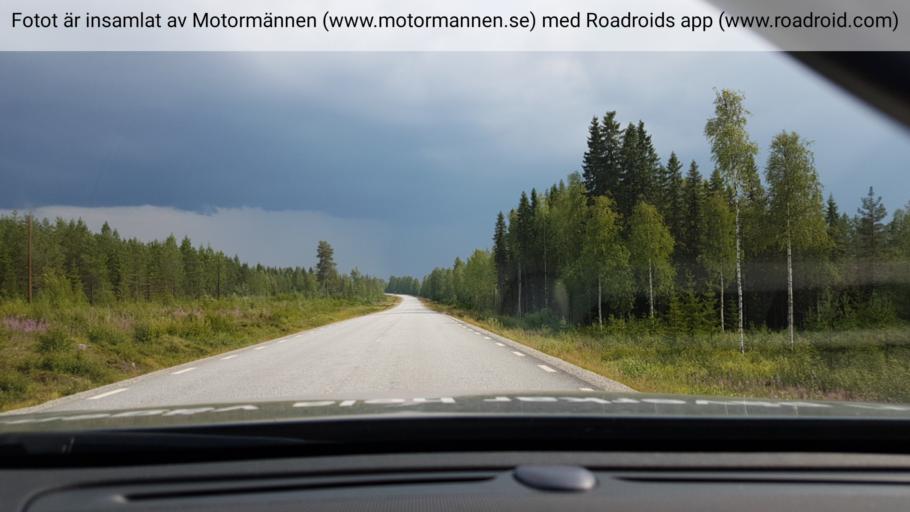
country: SE
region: Vaesterbotten
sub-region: Vindelns Kommun
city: Vindeln
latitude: 64.1934
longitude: 19.4592
